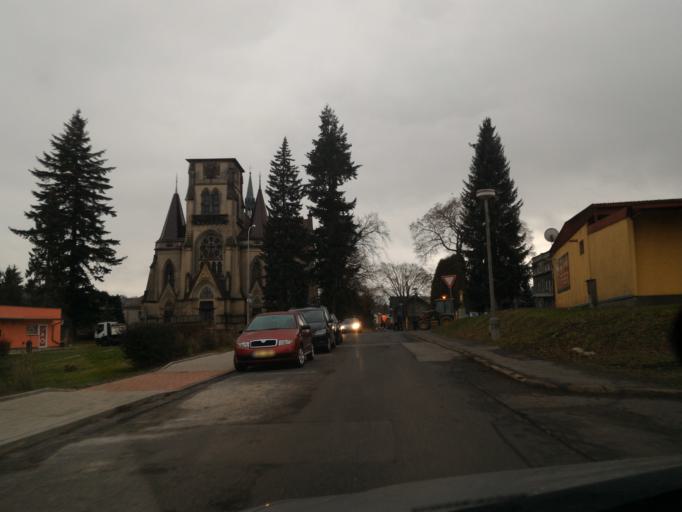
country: CZ
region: Ustecky
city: Varnsdorf
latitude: 50.9015
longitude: 14.6249
